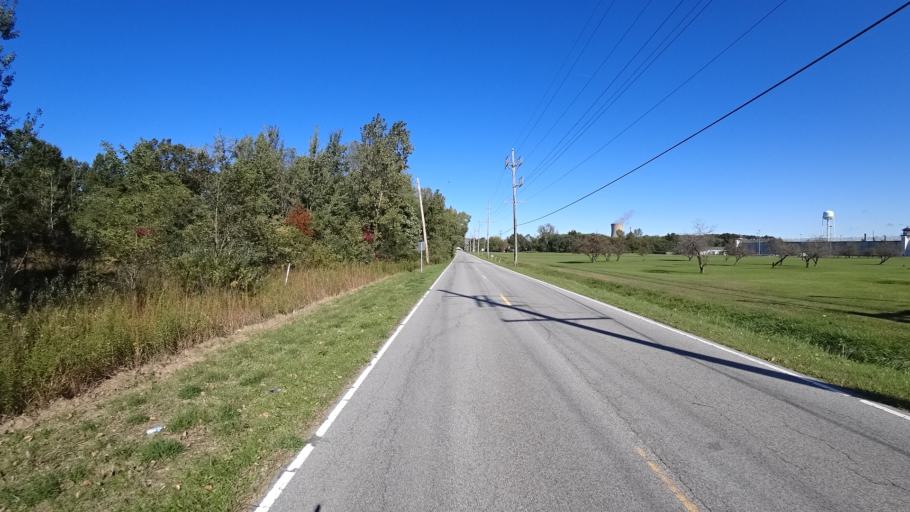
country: US
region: Indiana
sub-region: LaPorte County
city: Michigan City
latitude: 41.7027
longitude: -86.9219
